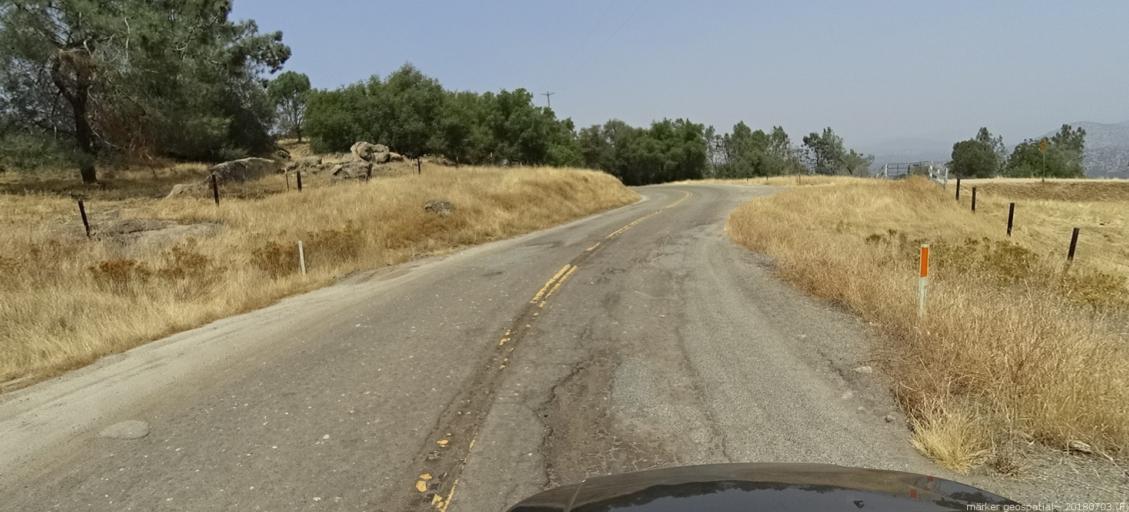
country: US
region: California
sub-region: Madera County
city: Yosemite Lakes
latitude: 37.0611
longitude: -119.6665
